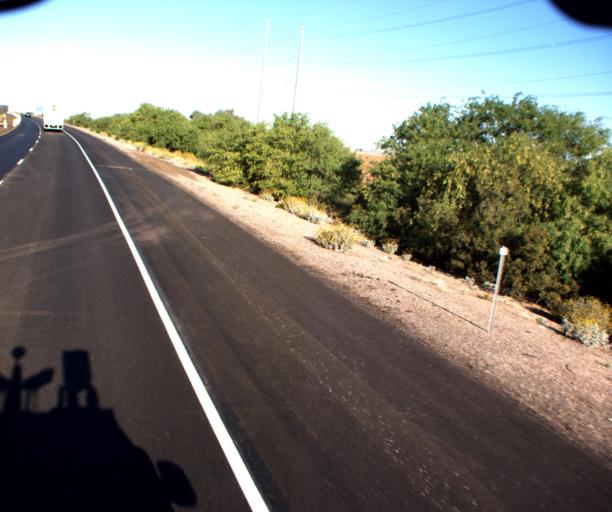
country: US
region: Arizona
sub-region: Pinal County
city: Casa Grande
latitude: 32.8348
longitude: -111.7141
